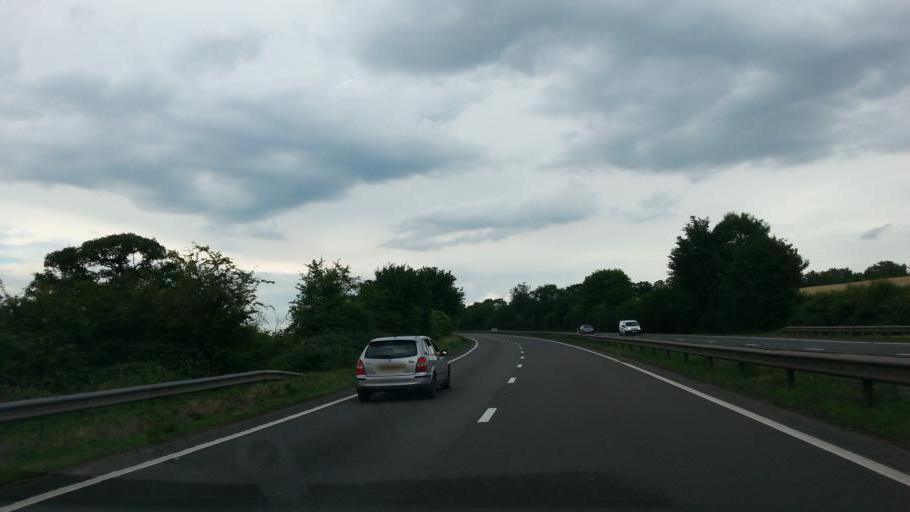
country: GB
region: England
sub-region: Herefordshire
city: Marstow
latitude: 51.8699
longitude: -2.6302
